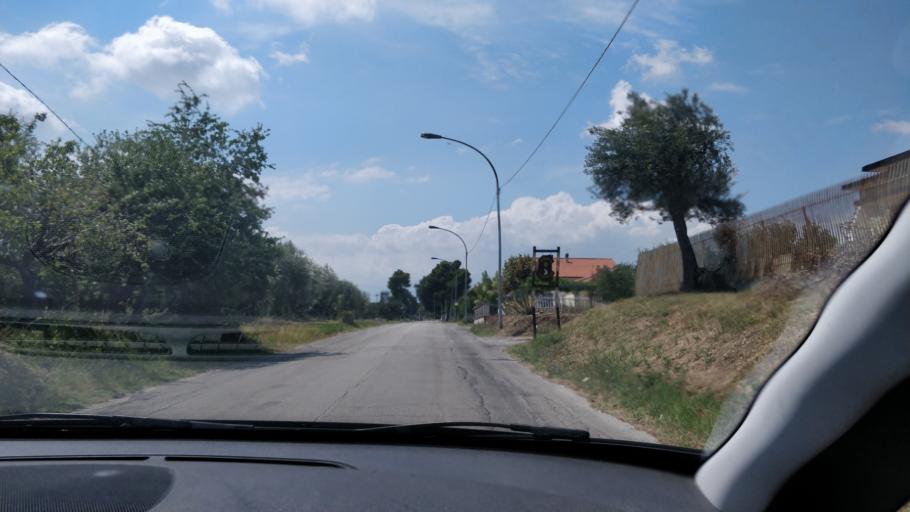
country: IT
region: Abruzzo
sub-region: Provincia di Chieti
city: Torrevecchia
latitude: 42.3971
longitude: 14.2084
